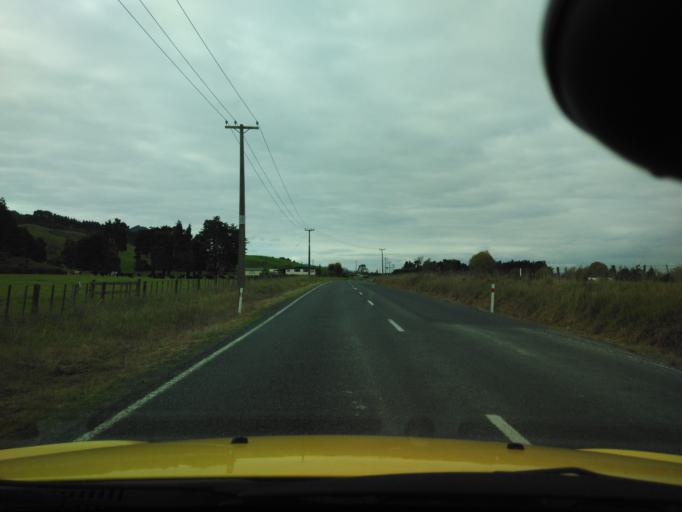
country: NZ
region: Waikato
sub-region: Waikato District
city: Ngaruawahia
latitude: -37.6295
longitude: 175.1638
